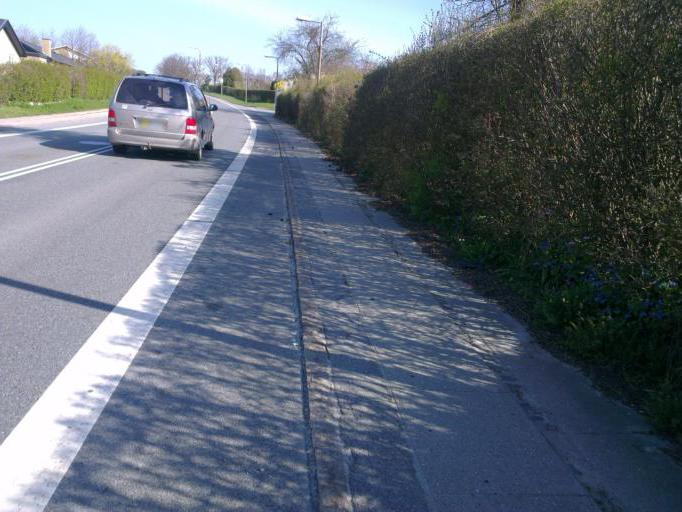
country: DK
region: Capital Region
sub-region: Frederikssund Kommune
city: Frederikssund
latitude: 55.8406
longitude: 12.0751
